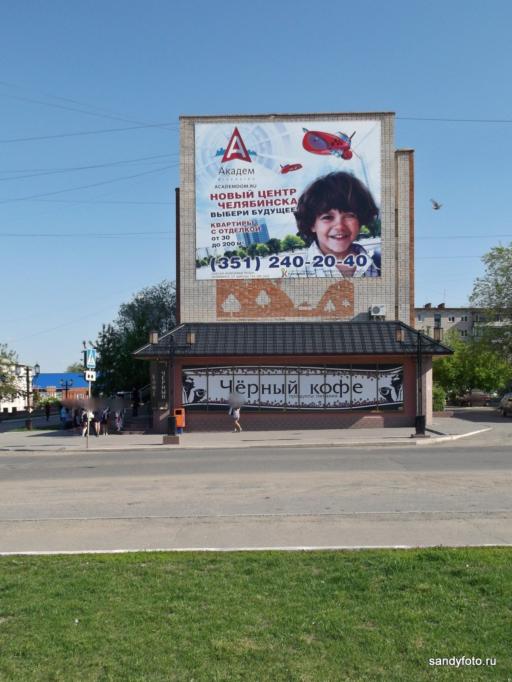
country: RU
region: Chelyabinsk
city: Troitsk
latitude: 54.0835
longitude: 61.5411
